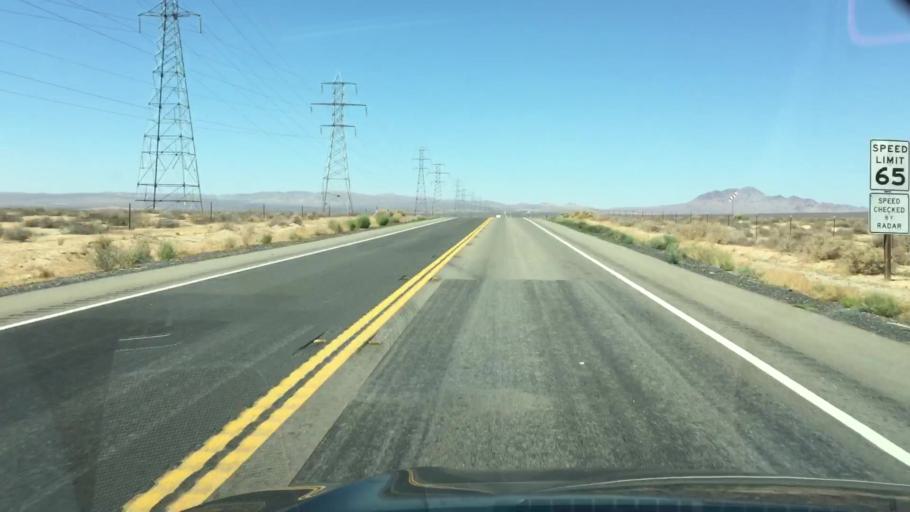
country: US
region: California
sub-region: Kern County
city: Boron
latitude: 35.1612
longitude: -117.5886
